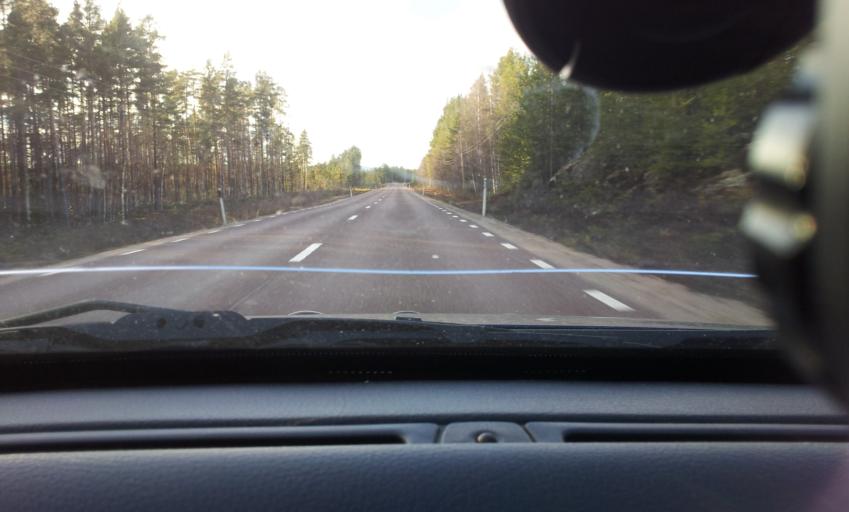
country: SE
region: Jaemtland
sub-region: Harjedalens Kommun
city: Sveg
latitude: 62.1389
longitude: 14.9654
